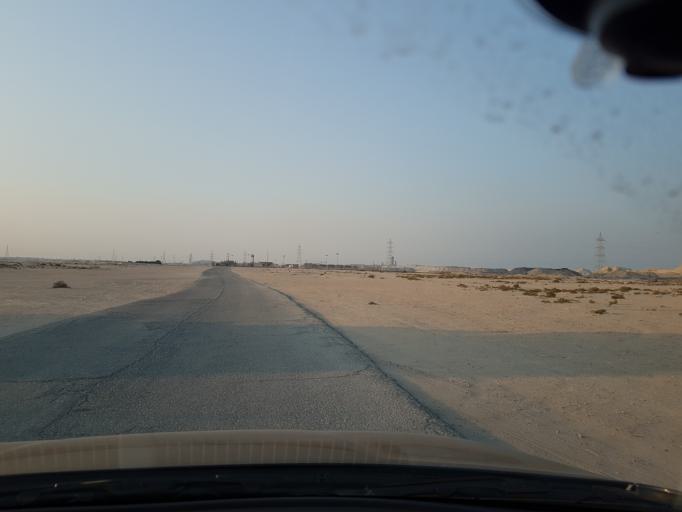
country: BH
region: Central Governorate
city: Dar Kulayb
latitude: 26.0021
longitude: 50.5854
